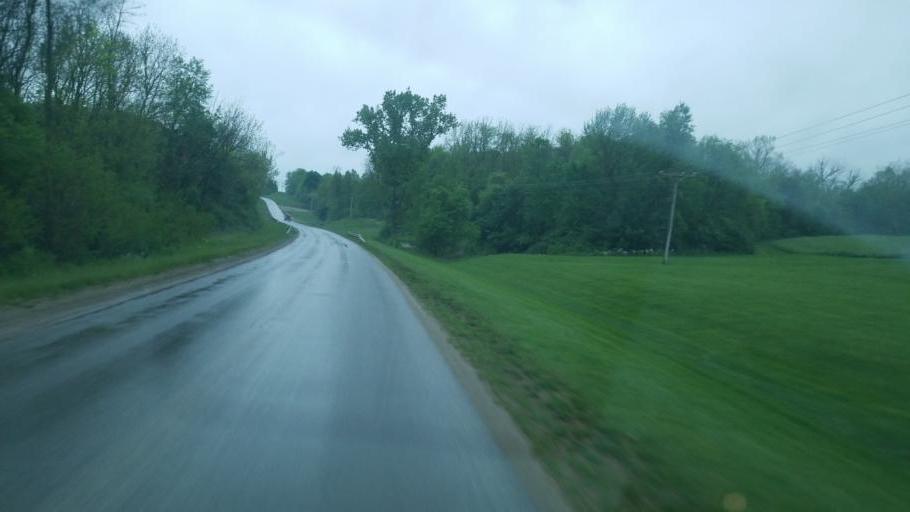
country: US
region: Ohio
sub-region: Highland County
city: Greenfield
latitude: 39.2949
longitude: -83.4631
